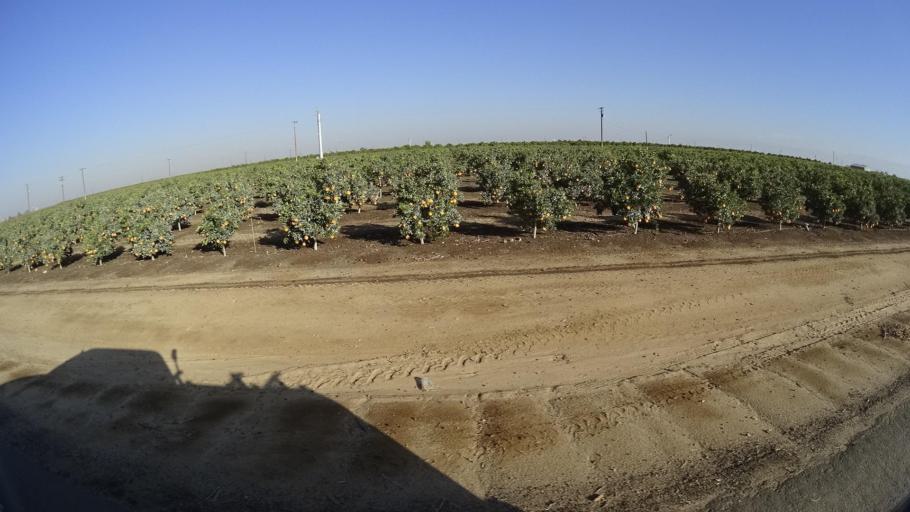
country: US
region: California
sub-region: Tulare County
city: Richgrove
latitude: 35.7687
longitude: -119.1591
